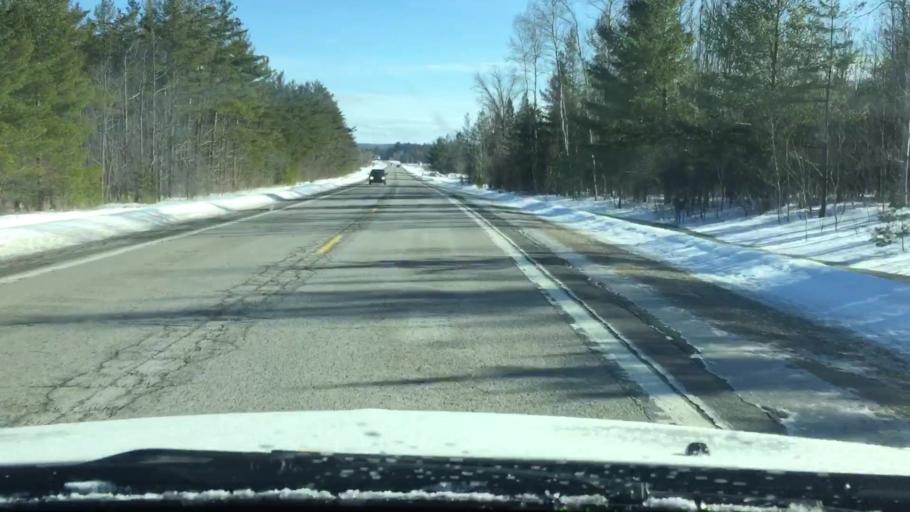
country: US
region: Michigan
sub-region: Charlevoix County
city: East Jordan
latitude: 45.1047
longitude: -85.1223
